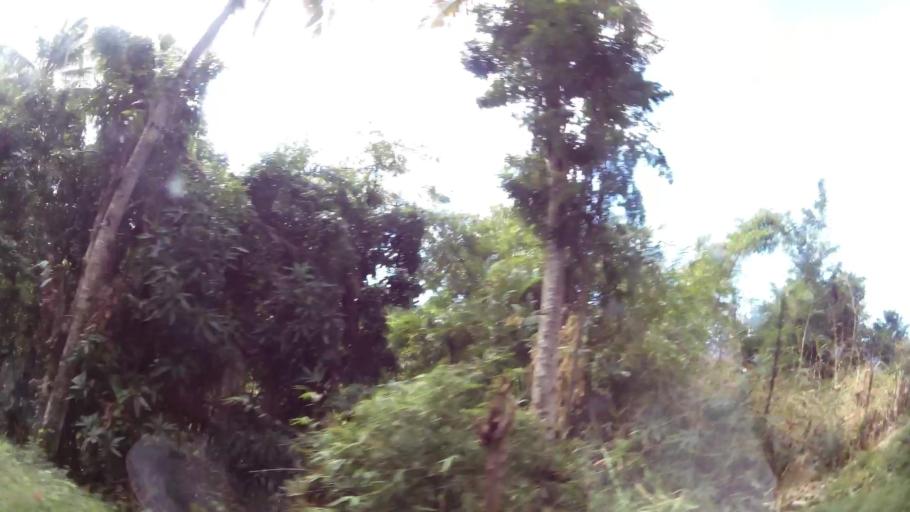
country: DM
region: Saint John
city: Portsmouth
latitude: 15.6298
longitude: -61.4622
